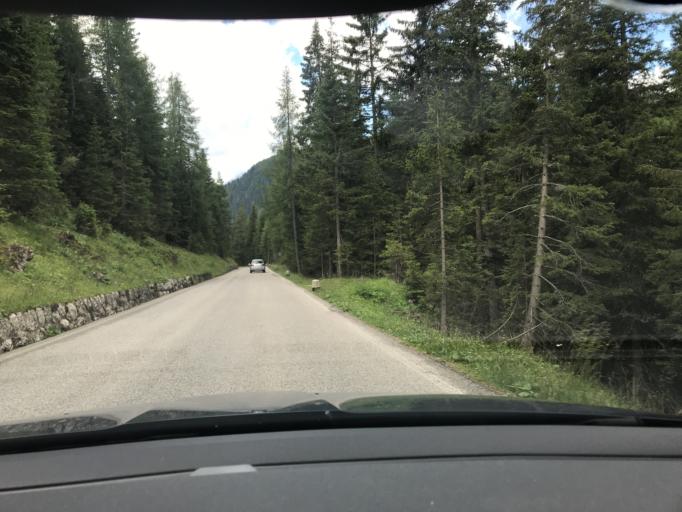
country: IT
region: Veneto
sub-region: Provincia di Belluno
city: Livinallongo del Col di Lana
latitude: 46.5047
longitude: 11.9969
